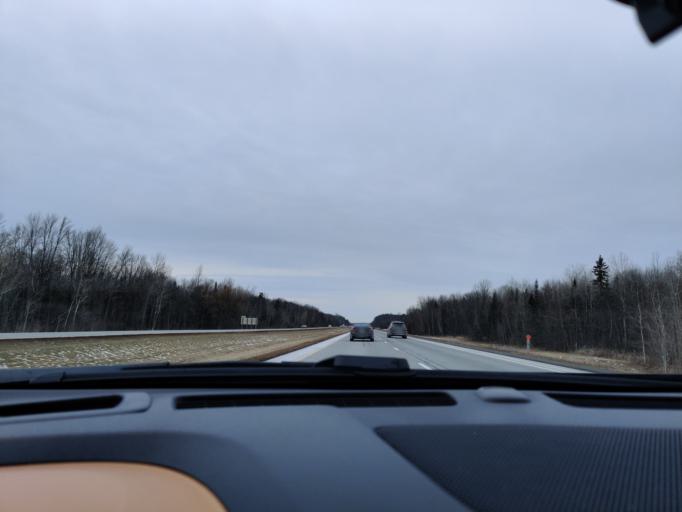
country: US
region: New York
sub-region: St. Lawrence County
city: Ogdensburg
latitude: 44.7957
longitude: -75.4295
